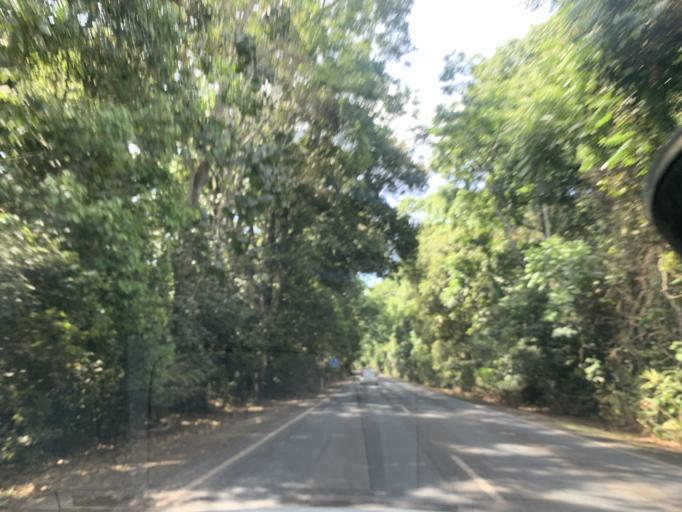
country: AU
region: Queensland
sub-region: Tablelands
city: Tolga
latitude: -17.2364
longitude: 145.4795
